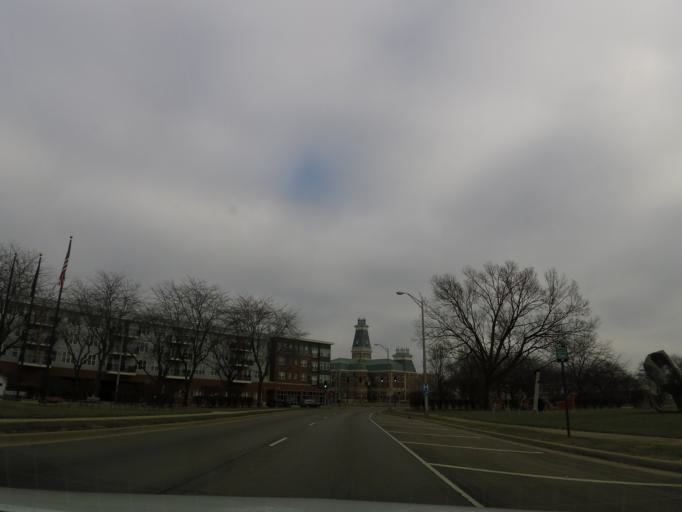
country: US
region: Indiana
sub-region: Bartholomew County
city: Columbus
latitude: 39.1996
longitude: -85.9235
